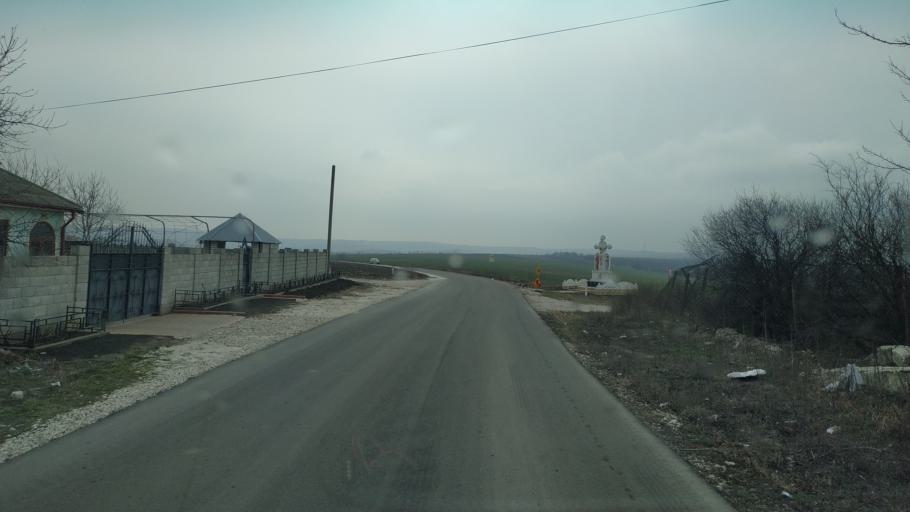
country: MD
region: Chisinau
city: Singera
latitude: 46.9012
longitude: 28.9871
